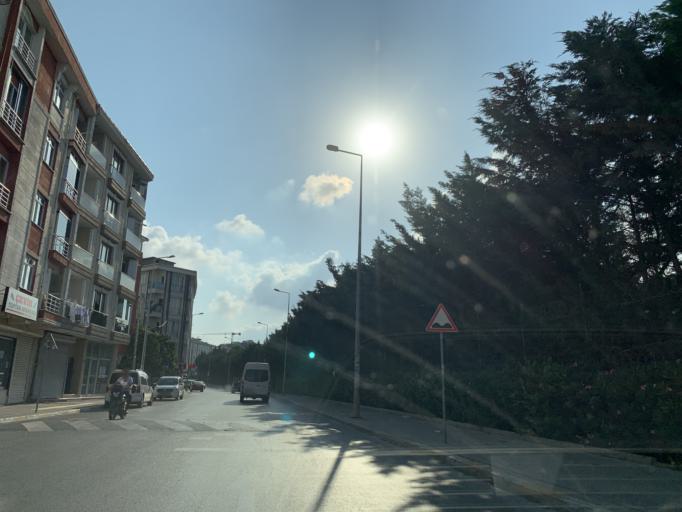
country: TR
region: Istanbul
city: Esenyurt
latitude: 41.0465
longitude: 28.6839
